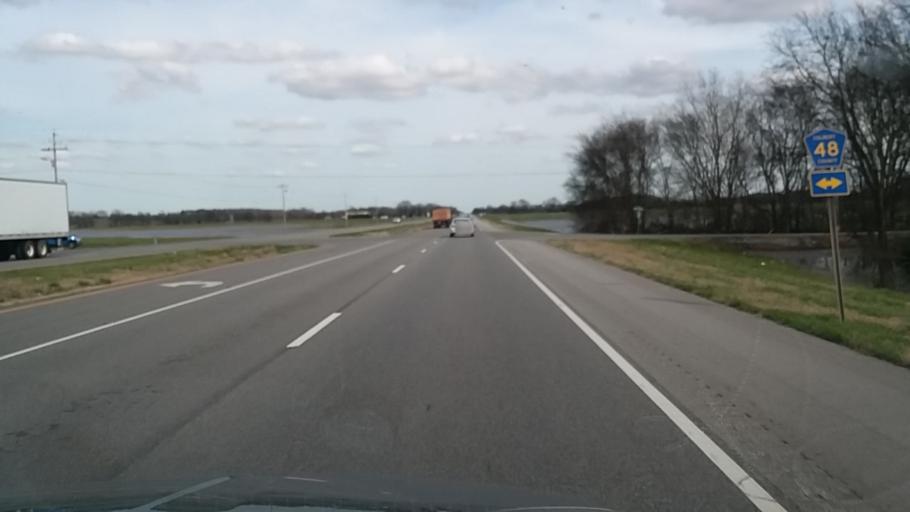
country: US
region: Alabama
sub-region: Lawrence County
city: Town Creek
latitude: 34.6838
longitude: -87.5295
